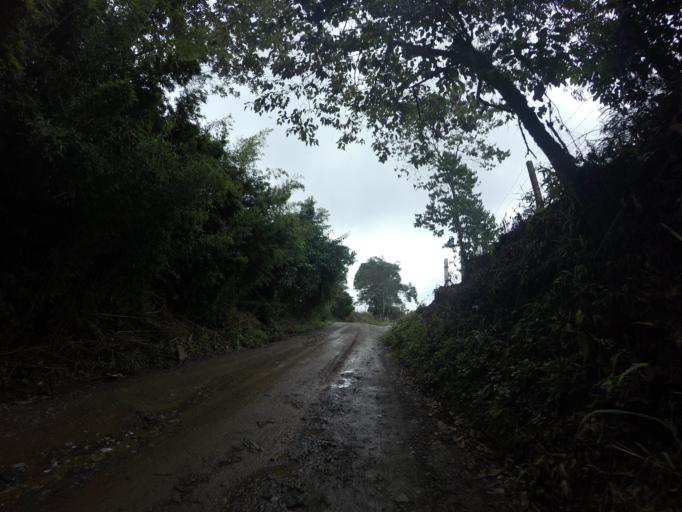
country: CO
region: Caldas
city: Victoria
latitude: 5.3234
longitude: -74.9388
